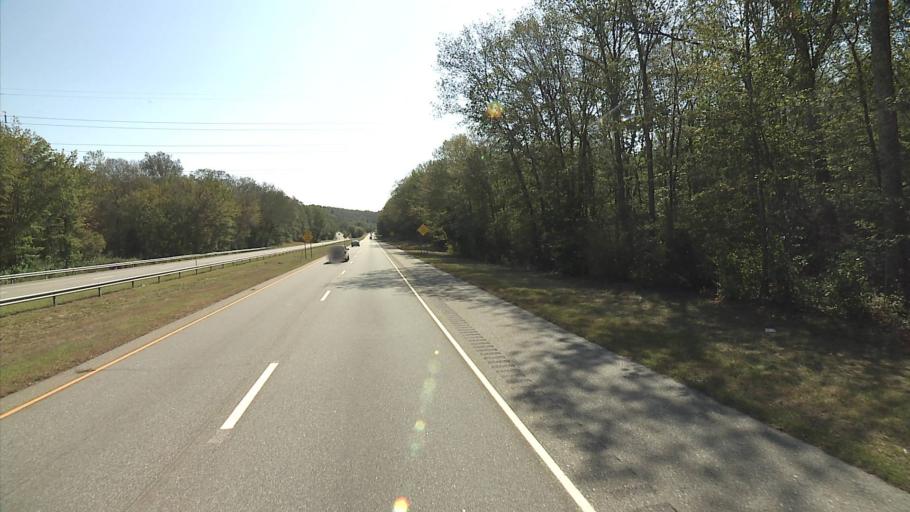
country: US
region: Connecticut
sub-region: New London County
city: Uncasville
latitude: 41.4228
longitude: -72.1180
